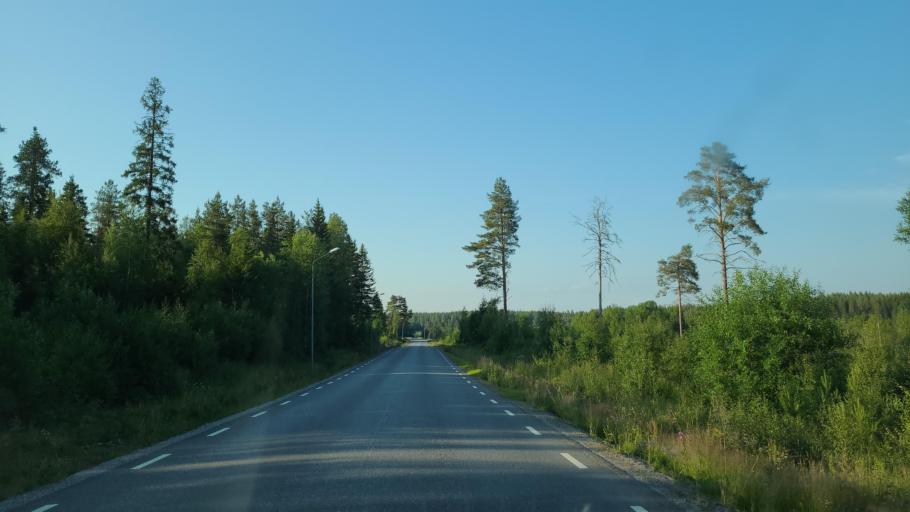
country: SE
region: Vaesterbotten
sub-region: Skelleftea Kommun
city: Burea
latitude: 64.4507
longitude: 21.3542
